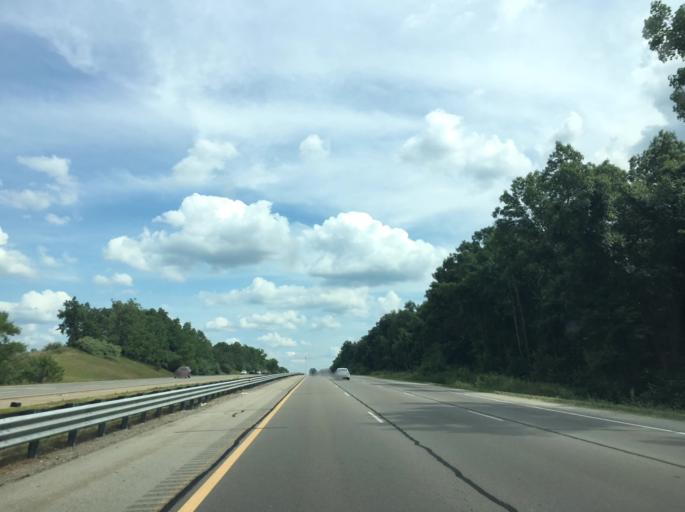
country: US
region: Michigan
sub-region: Oakland County
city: Holly
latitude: 42.8315
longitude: -83.5769
